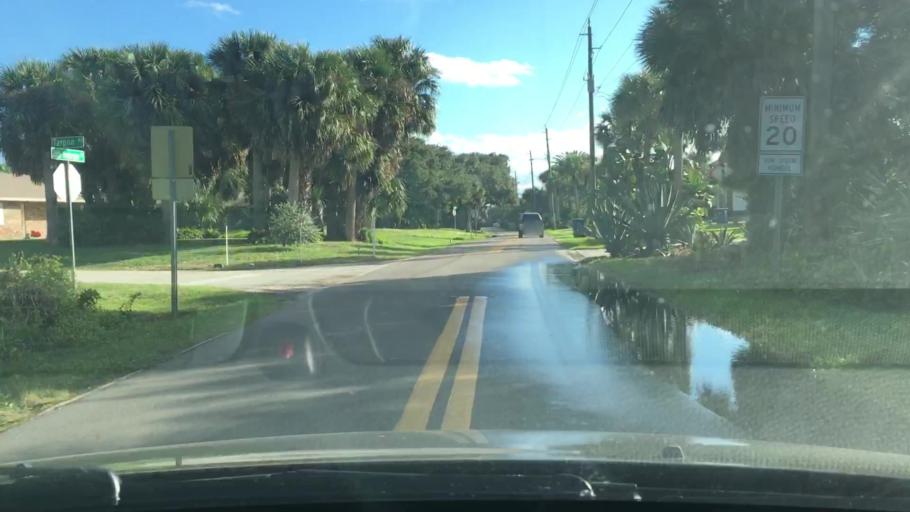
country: US
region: Florida
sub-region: Volusia County
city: Ormond-by-the-Sea
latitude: 29.3842
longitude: -81.0878
